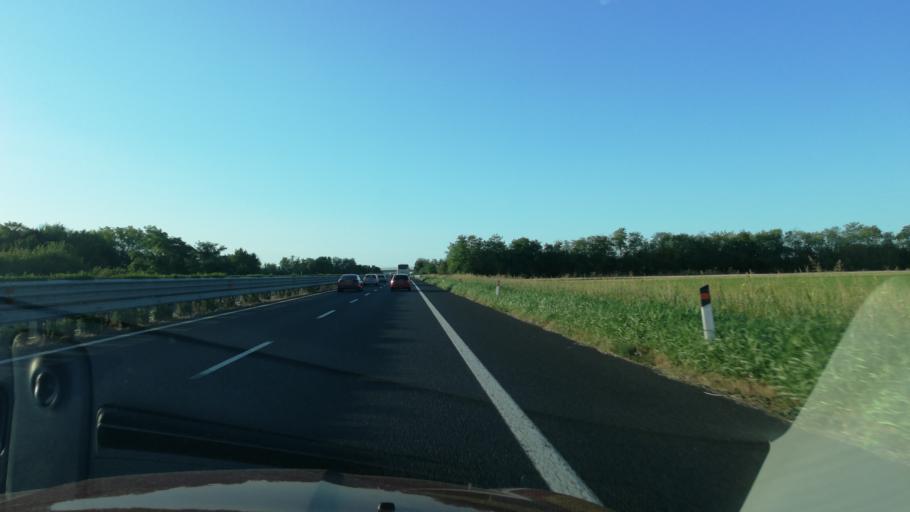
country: IT
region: Friuli Venezia Giulia
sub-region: Provincia di Udine
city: Zugliano-Terenzano-Cargnacco
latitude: 45.9926
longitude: 13.2350
